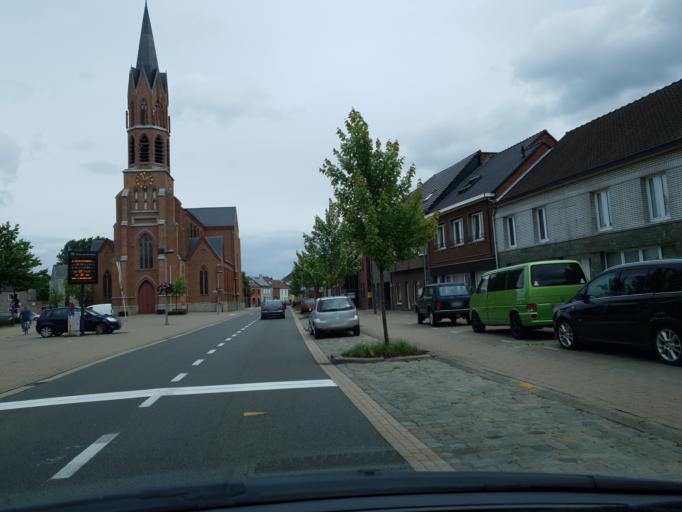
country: BE
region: Flanders
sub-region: Provincie Antwerpen
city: Hulshout
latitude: 51.0523
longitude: 4.7779
